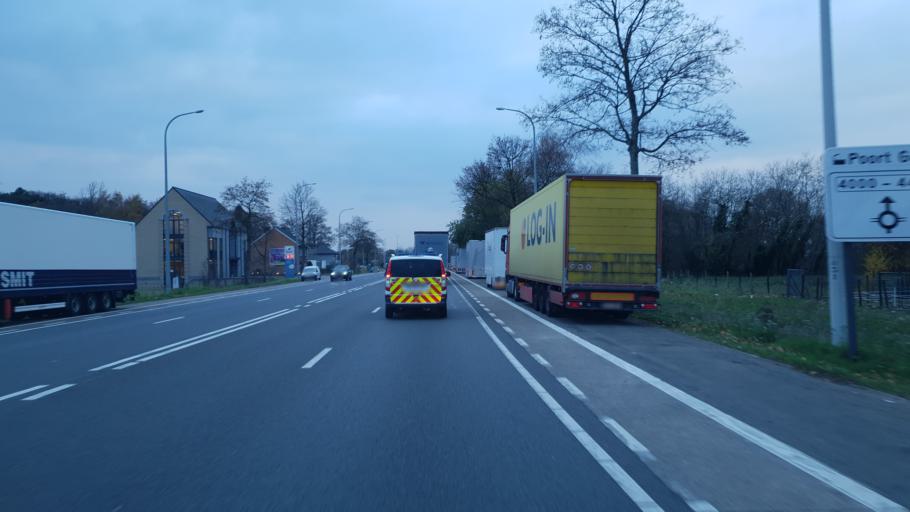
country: BE
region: Flanders
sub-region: Provincie Limburg
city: Diepenbeek
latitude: 50.9204
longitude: 5.4441
